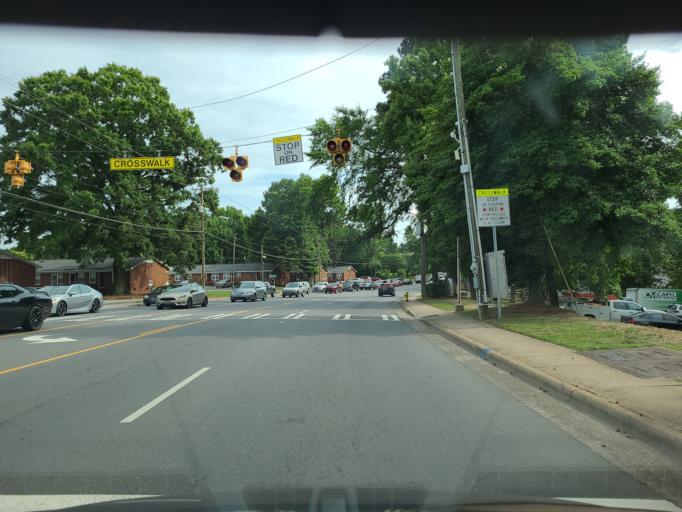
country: US
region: North Carolina
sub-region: Mecklenburg County
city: Charlotte
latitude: 35.2069
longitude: -80.7582
